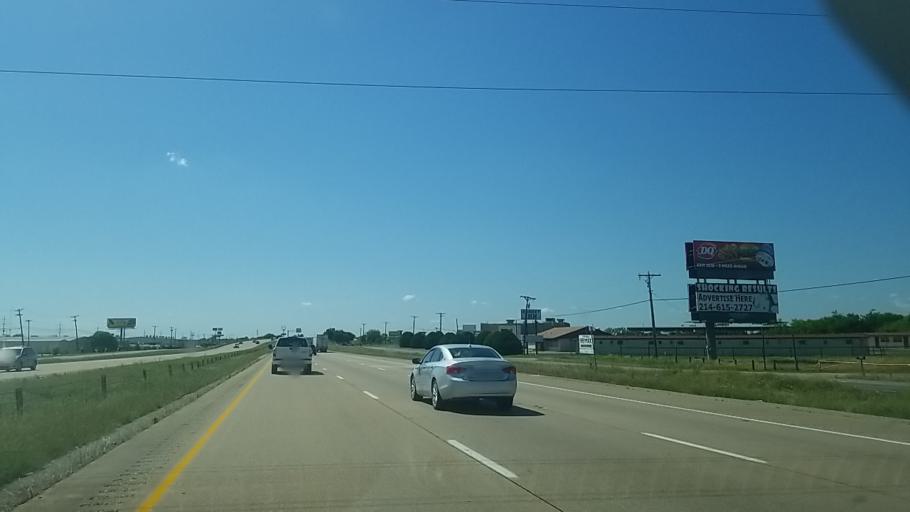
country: US
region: Texas
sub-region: Ellis County
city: Ennis
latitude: 32.3078
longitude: -96.5910
